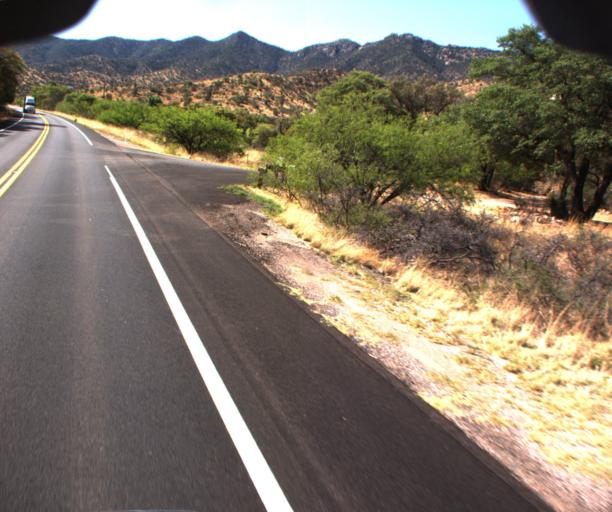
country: US
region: Arizona
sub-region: Cochise County
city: Bisbee
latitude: 31.4921
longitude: -109.9904
